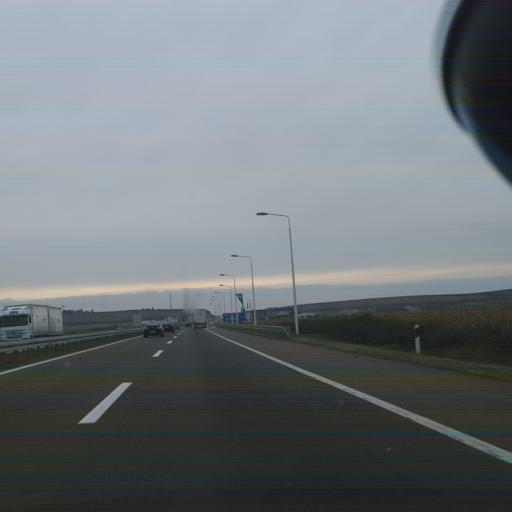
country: RS
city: Beska
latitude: 45.1423
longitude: 20.0853
